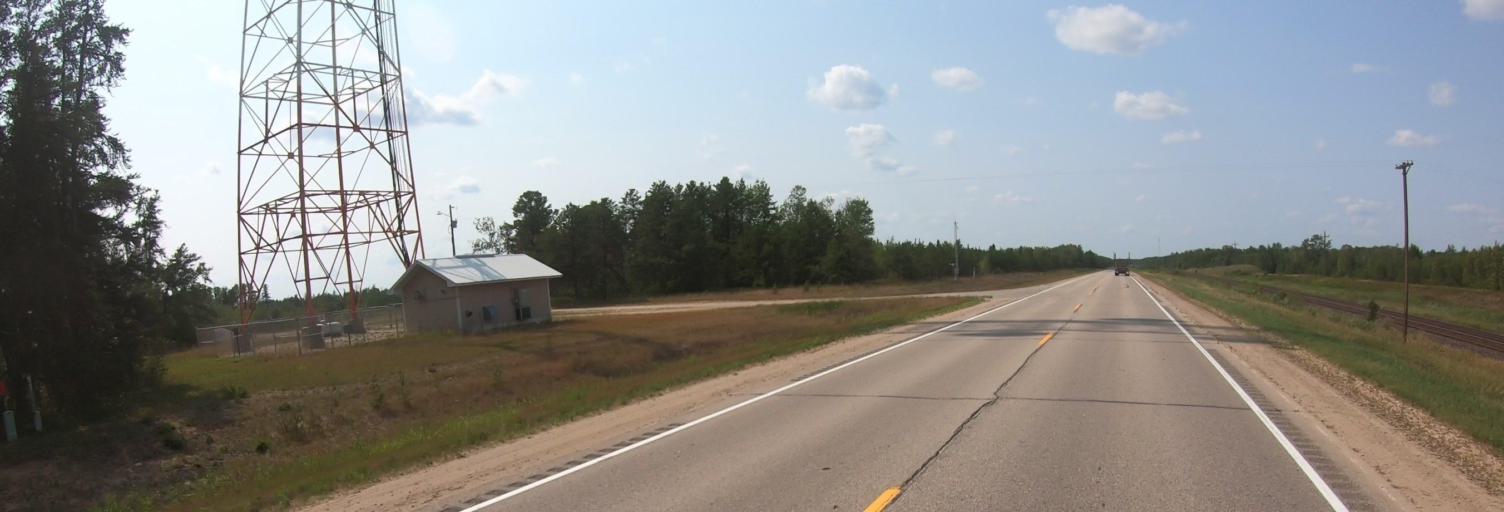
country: US
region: Minnesota
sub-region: Roseau County
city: Warroad
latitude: 48.7894
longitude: -95.0493
